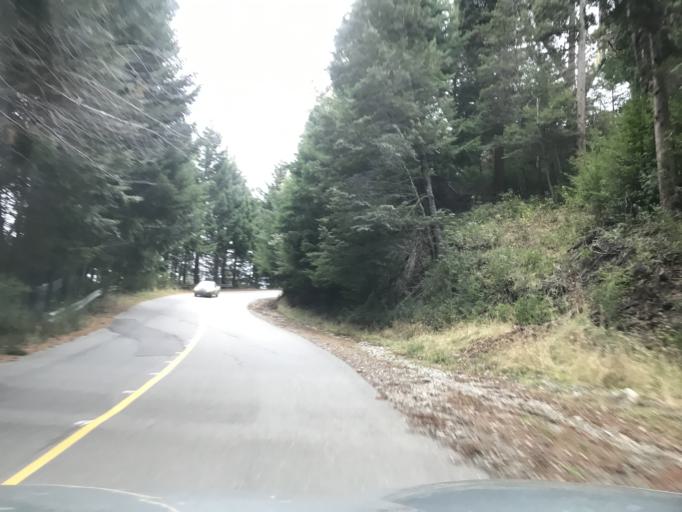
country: AR
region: Rio Negro
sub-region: Departamento de Bariloche
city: San Carlos de Bariloche
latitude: -41.0771
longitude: -71.5451
